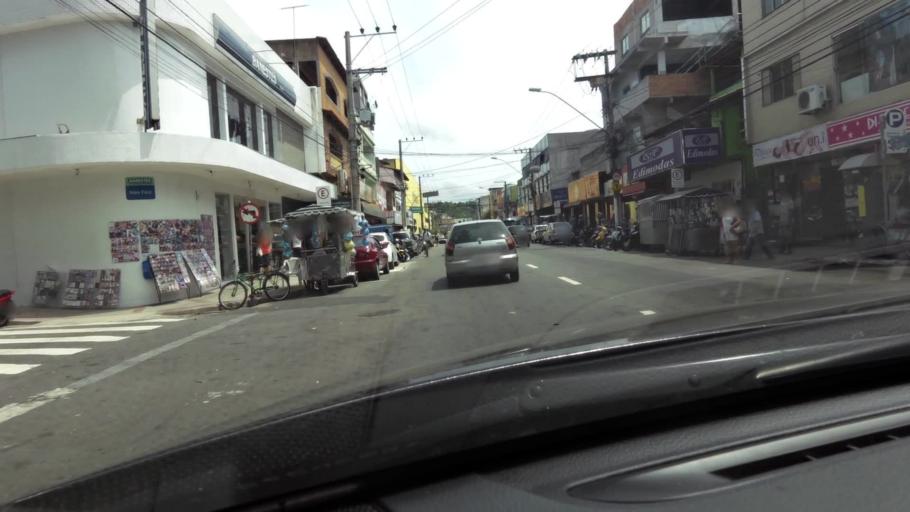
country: BR
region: Espirito Santo
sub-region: Vila Velha
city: Vila Velha
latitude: -20.3373
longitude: -40.3076
